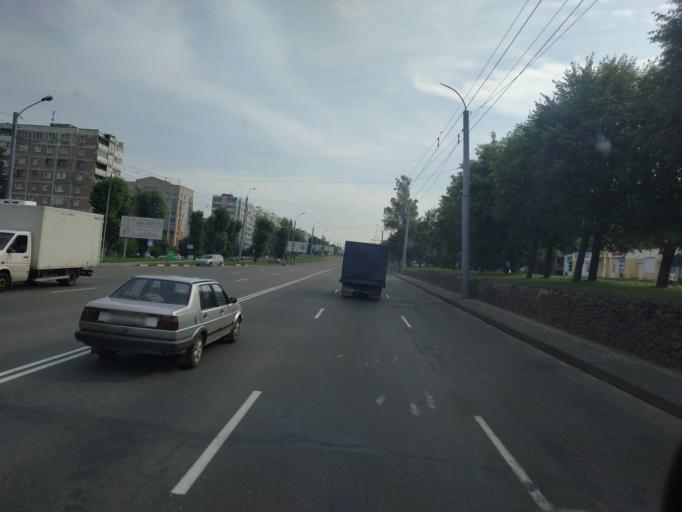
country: BY
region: Mogilev
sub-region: Mahilyowski Rayon
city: Veyno
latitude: 53.8726
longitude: 30.3728
